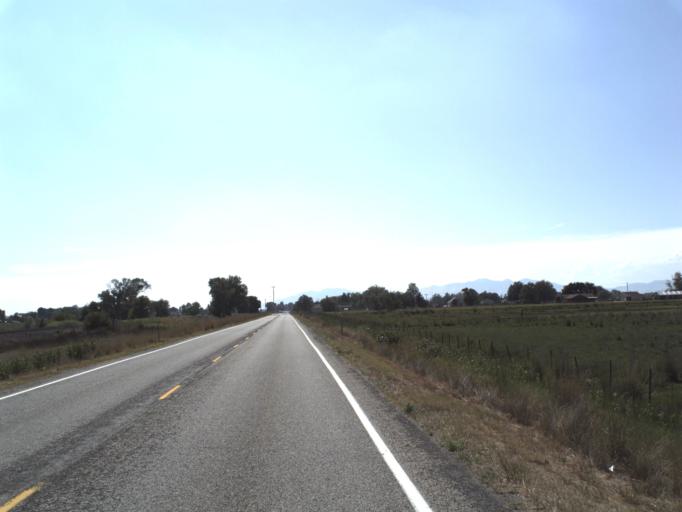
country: US
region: Utah
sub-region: Weber County
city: Marriott-Slaterville
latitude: 41.2444
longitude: -112.0687
